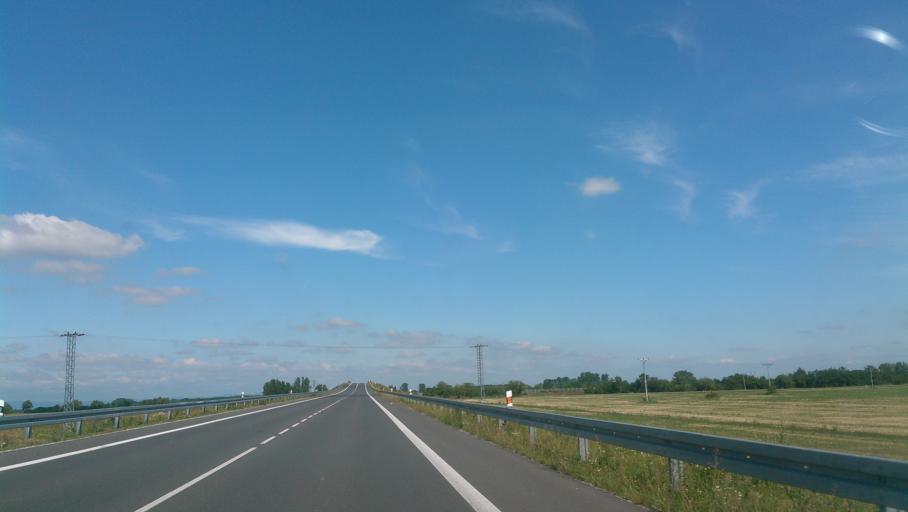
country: SK
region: Trnavsky
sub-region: Okres Galanta
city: Galanta
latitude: 48.1820
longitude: 17.7032
